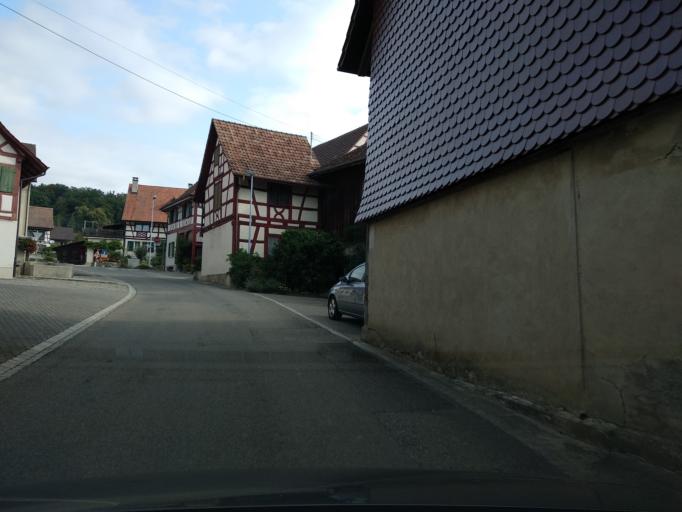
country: CH
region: Zurich
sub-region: Bezirk Andelfingen
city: Marthalen
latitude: 47.6511
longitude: 8.6758
